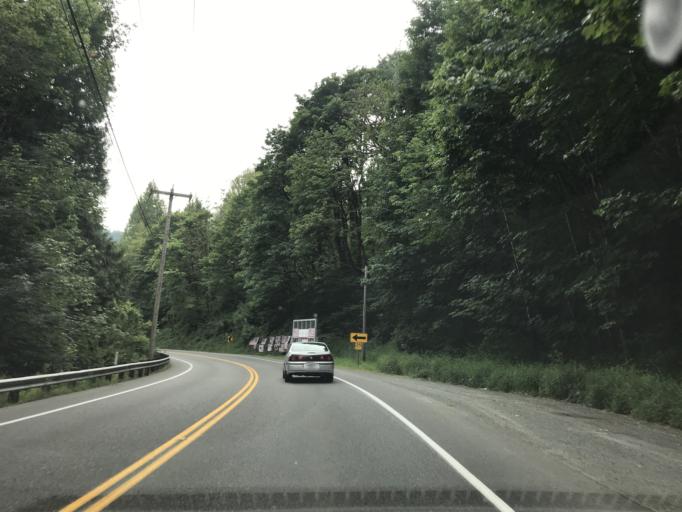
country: US
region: Washington
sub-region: King County
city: Fall City
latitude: 47.5268
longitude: -121.9260
